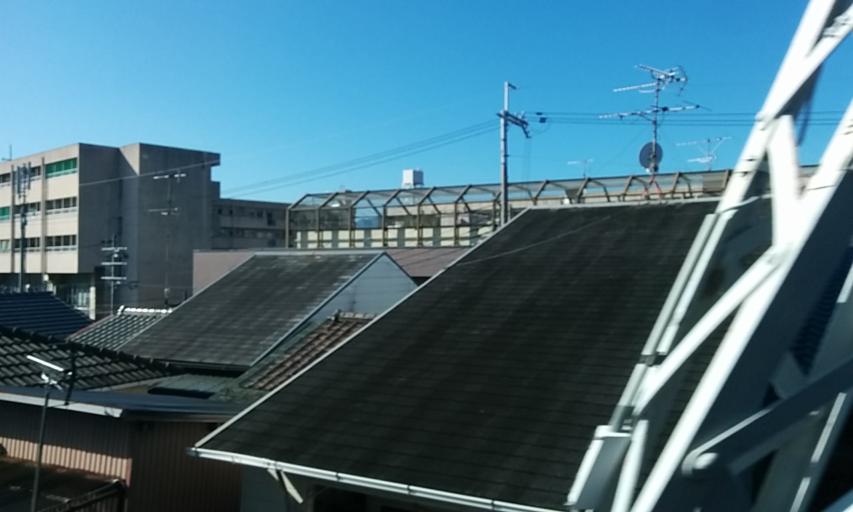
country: JP
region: Kyoto
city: Muko
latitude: 34.9867
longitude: 135.6999
